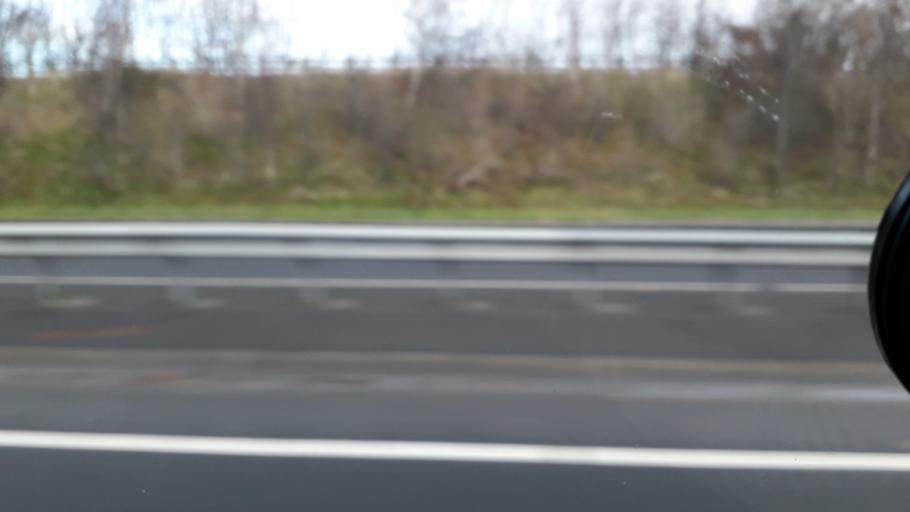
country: IE
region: Leinster
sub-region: An Mhi
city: Ashbourne
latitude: 53.4908
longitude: -6.4027
